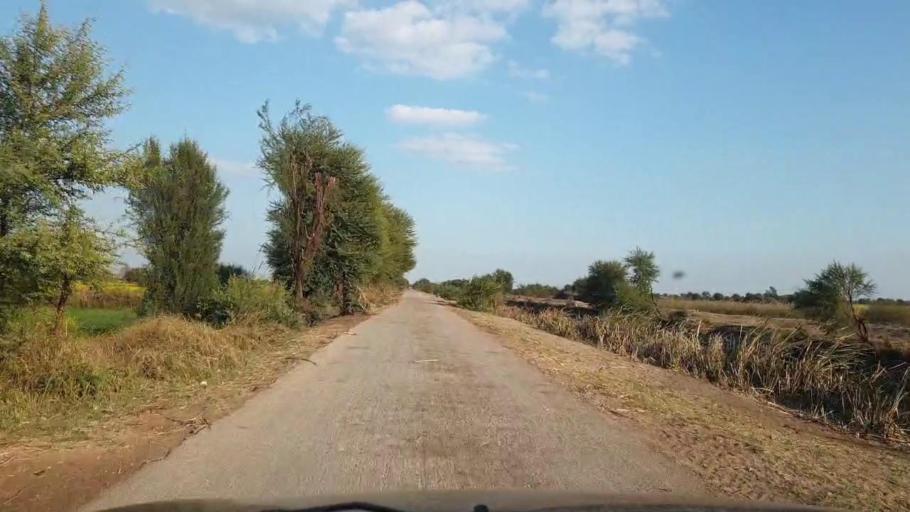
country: PK
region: Sindh
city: Sinjhoro
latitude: 25.9956
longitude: 68.7406
